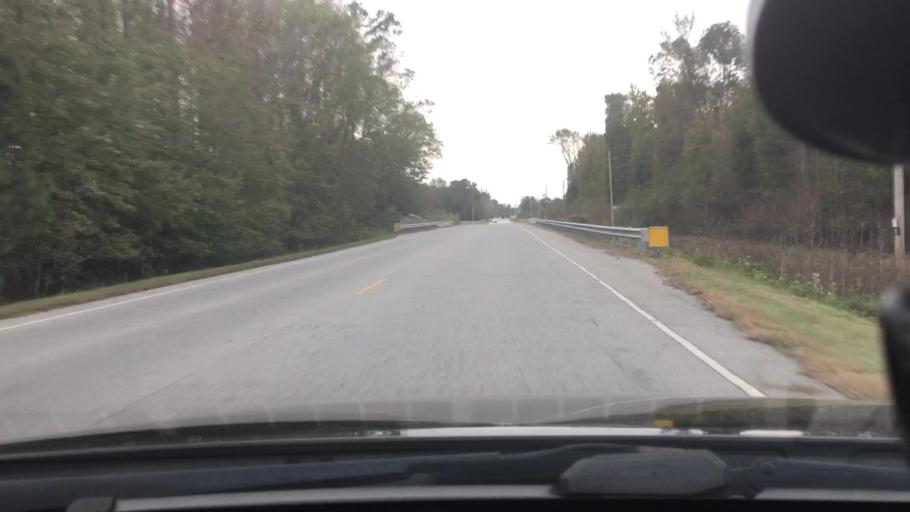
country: US
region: North Carolina
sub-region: Pitt County
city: Windsor
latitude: 35.4566
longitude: -77.2677
